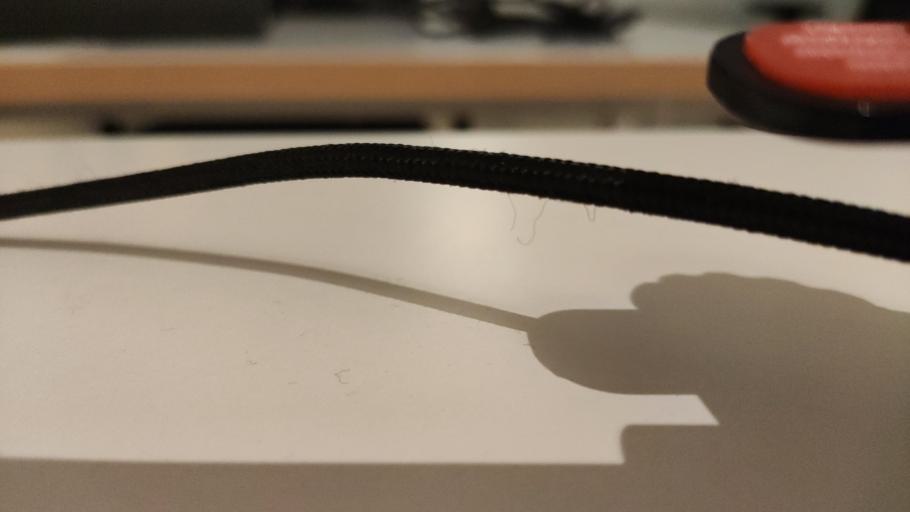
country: RU
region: Moskovskaya
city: Kurovskoye
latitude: 55.5894
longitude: 38.9155
